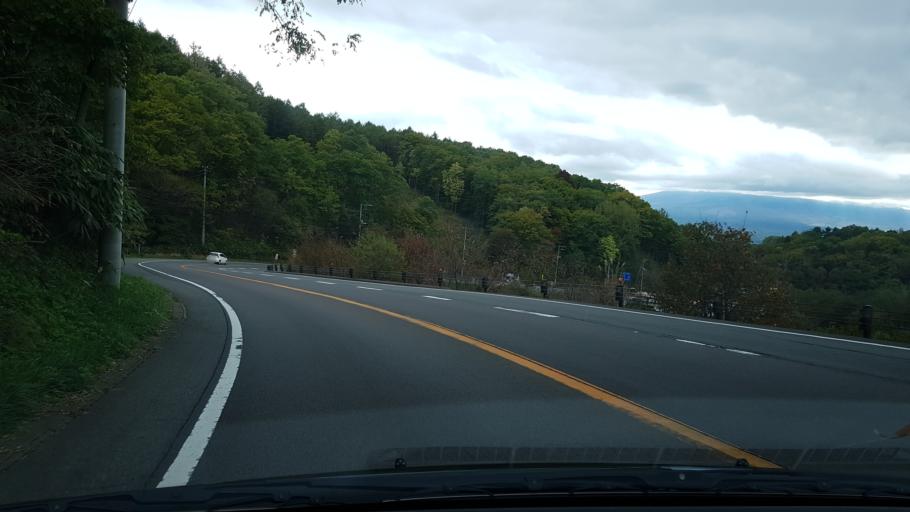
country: JP
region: Gunma
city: Nakanojomachi
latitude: 36.5989
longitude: 138.5867
